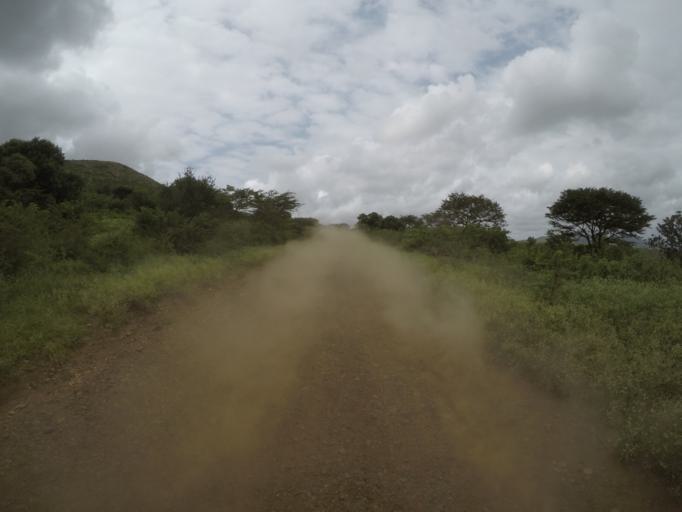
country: ZA
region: KwaZulu-Natal
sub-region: uThungulu District Municipality
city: Empangeni
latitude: -28.6028
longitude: 31.8937
